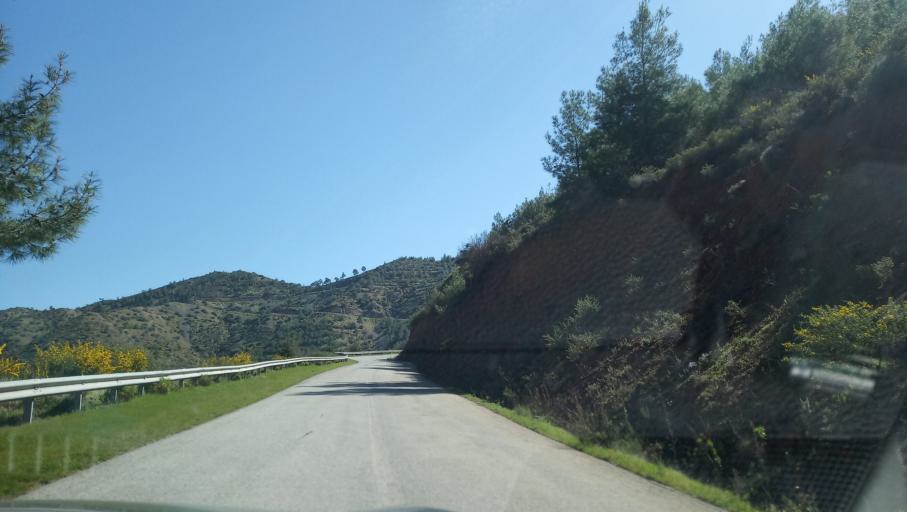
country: CY
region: Lefkosia
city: Lefka
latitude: 35.0738
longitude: 32.8093
